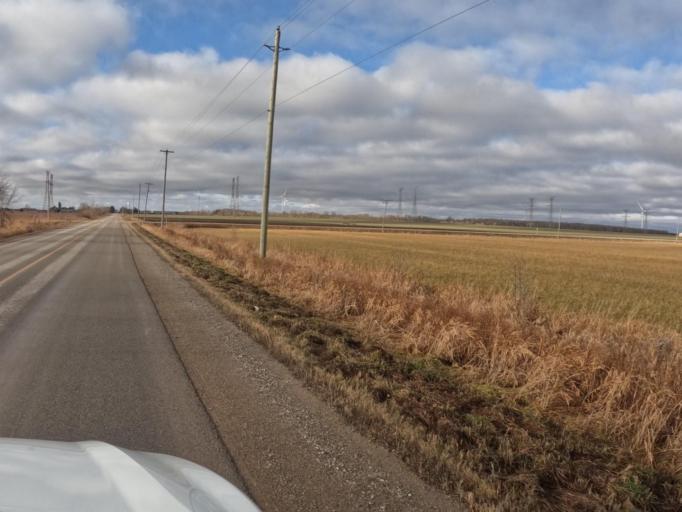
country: CA
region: Ontario
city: Shelburne
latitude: 43.8948
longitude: -80.3359
